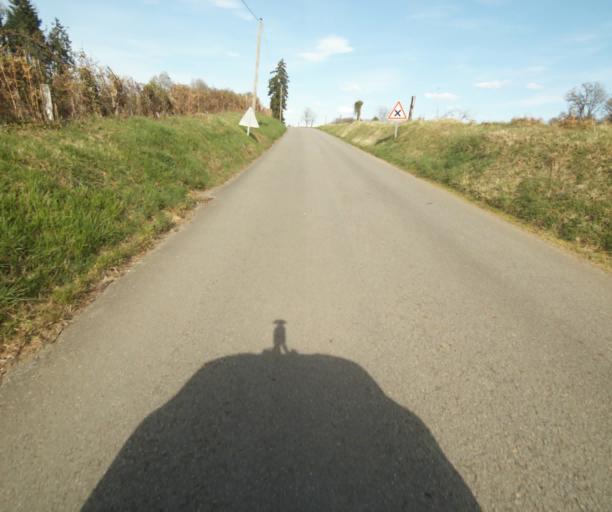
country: FR
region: Limousin
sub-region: Departement de la Correze
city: Naves
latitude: 45.3007
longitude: 1.7333
